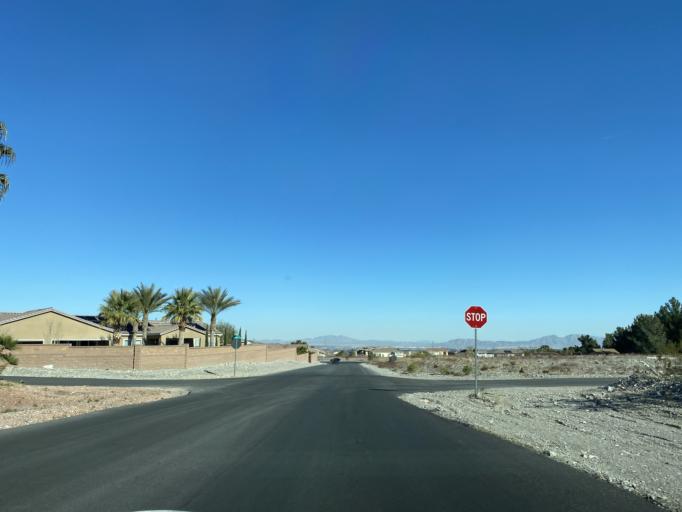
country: US
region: Nevada
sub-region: Clark County
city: Summerlin South
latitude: 36.2883
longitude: -115.3085
